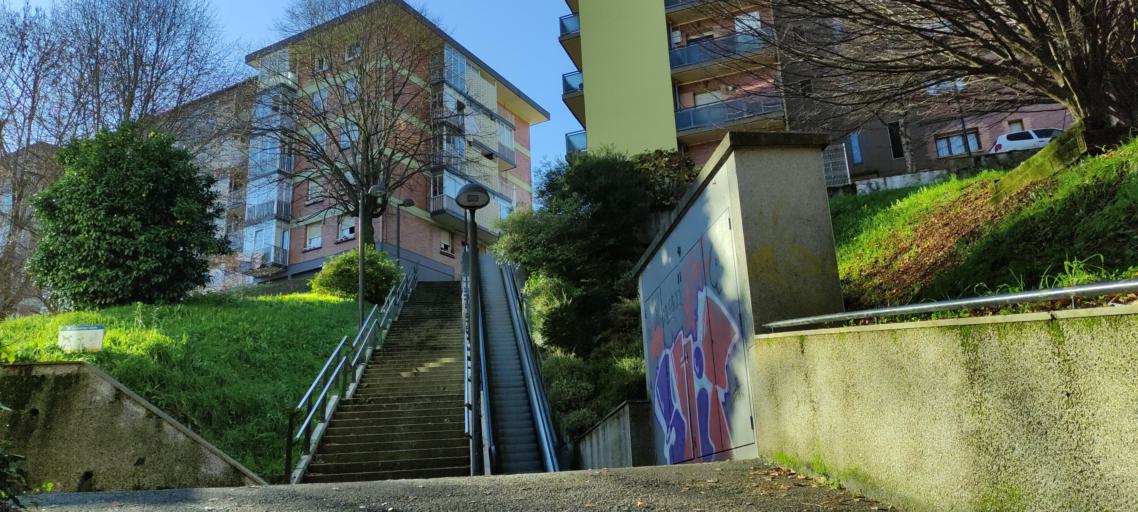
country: ES
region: Basque Country
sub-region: Provincia de Guipuzcoa
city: Andoain
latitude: 43.2228
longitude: -2.0234
